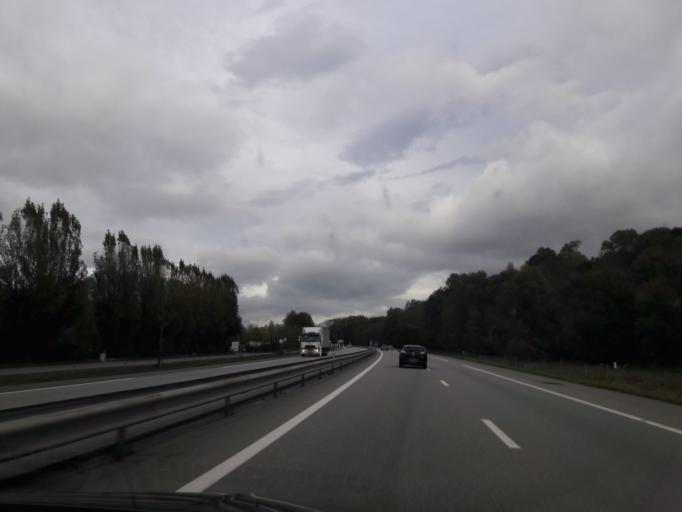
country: FR
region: Rhone-Alpes
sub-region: Departement de la Savoie
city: Montmelian
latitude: 45.4975
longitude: 6.0716
